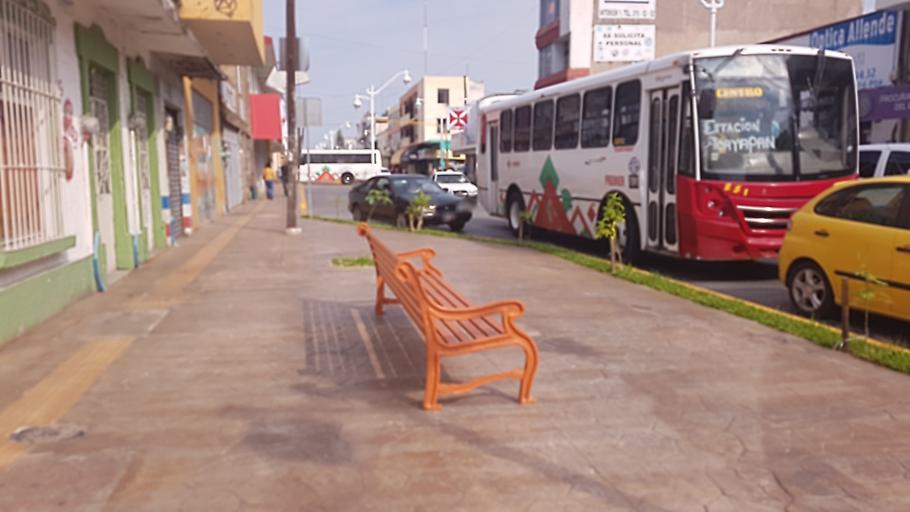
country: MX
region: Nayarit
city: Tepic
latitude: 21.5087
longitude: -104.8931
